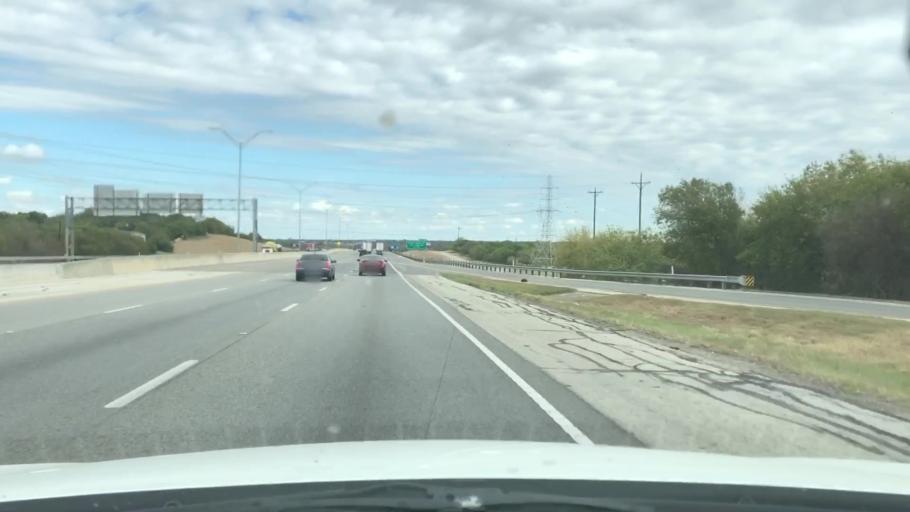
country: US
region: Texas
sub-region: Bexar County
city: San Antonio
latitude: 29.4039
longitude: -98.4423
